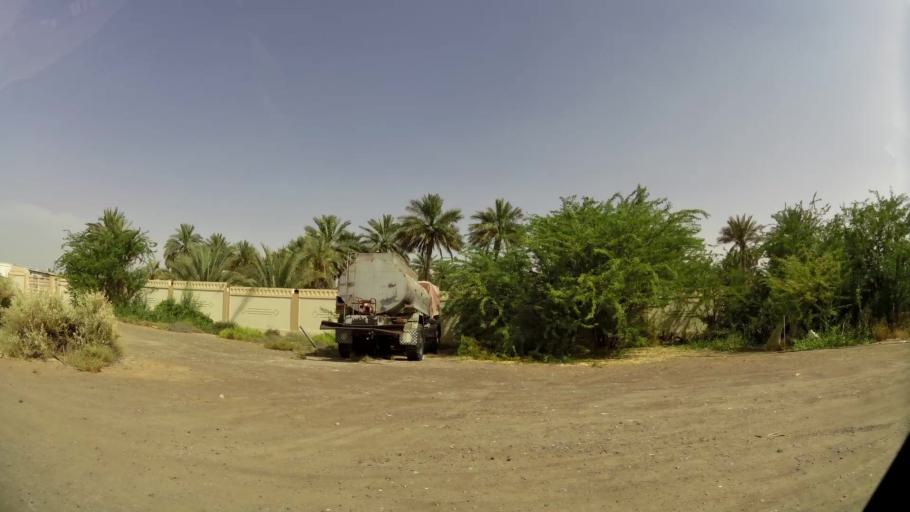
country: AE
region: Abu Dhabi
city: Al Ain
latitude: 24.2292
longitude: 55.6861
